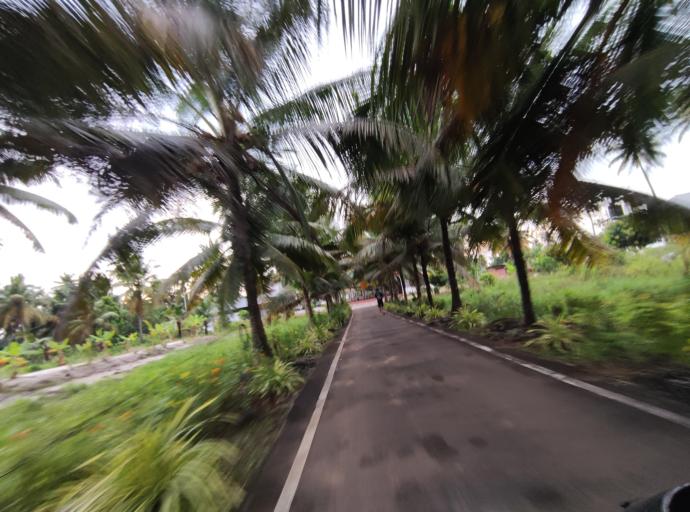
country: IN
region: Kerala
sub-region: Alappuzha
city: Shertallai
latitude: 9.6399
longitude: 76.4290
